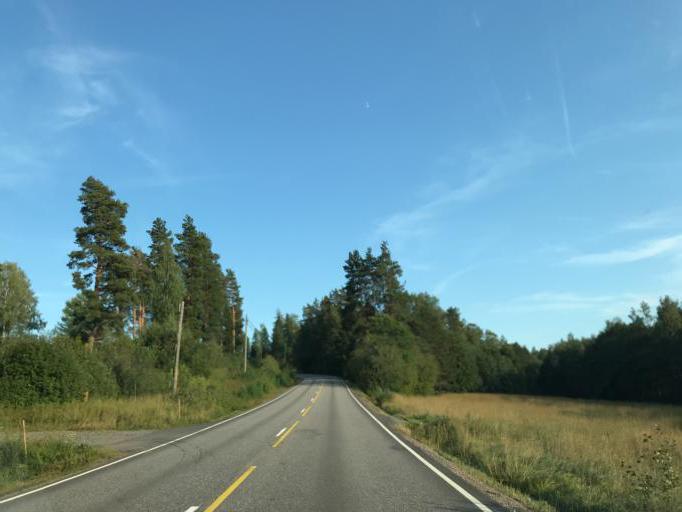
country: FI
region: Uusimaa
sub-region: Helsinki
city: Vihti
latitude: 60.4204
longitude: 24.3682
